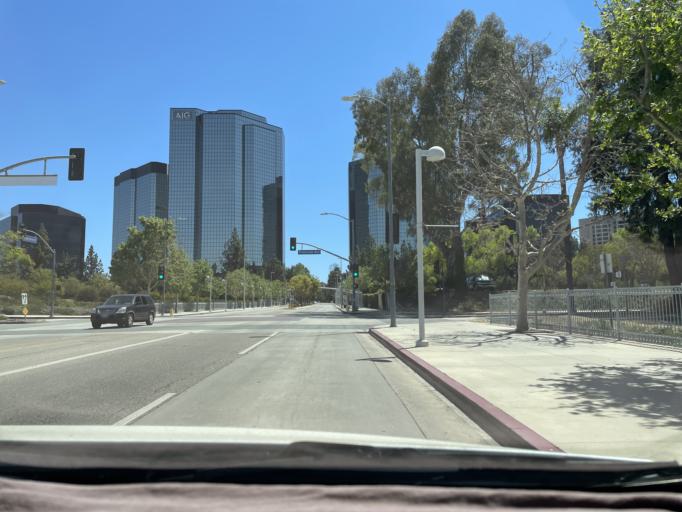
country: US
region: California
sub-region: Los Angeles County
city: Woodland Hills
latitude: 34.1815
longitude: -118.6016
